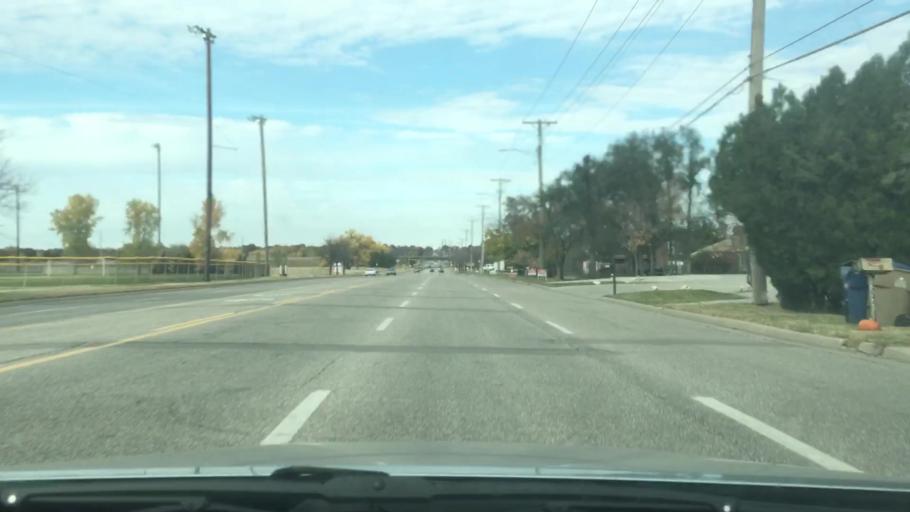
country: US
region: Kansas
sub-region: Sedgwick County
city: Wichita
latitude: 37.6375
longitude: -97.2804
